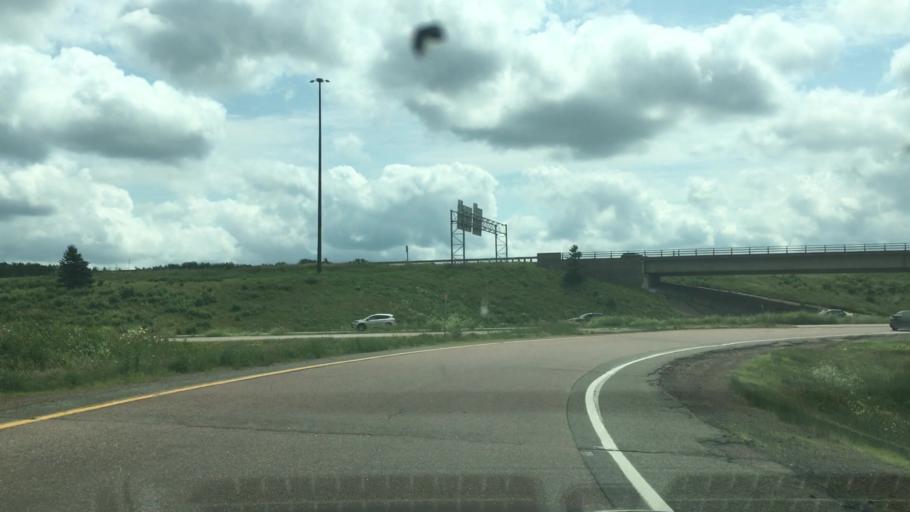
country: CA
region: New Brunswick
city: Dieppe
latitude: 46.1295
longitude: -64.6801
